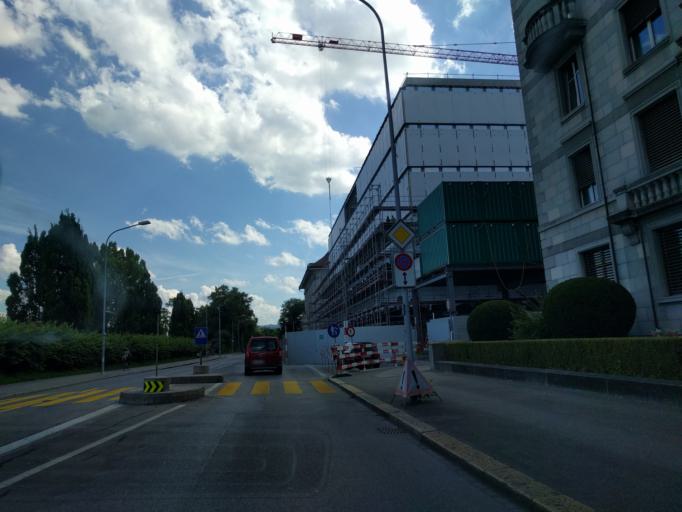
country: CH
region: Zurich
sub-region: Bezirk Zuerich
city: Zuerich (Kreis 2) / Enge
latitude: 47.3607
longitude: 8.5353
